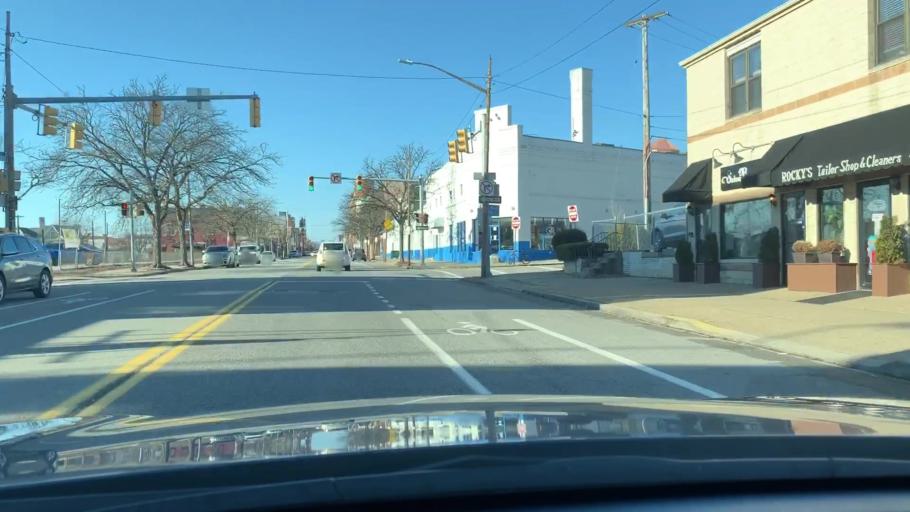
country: US
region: Pennsylvania
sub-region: Allegheny County
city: Bloomfield
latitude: 40.4587
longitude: -79.9435
